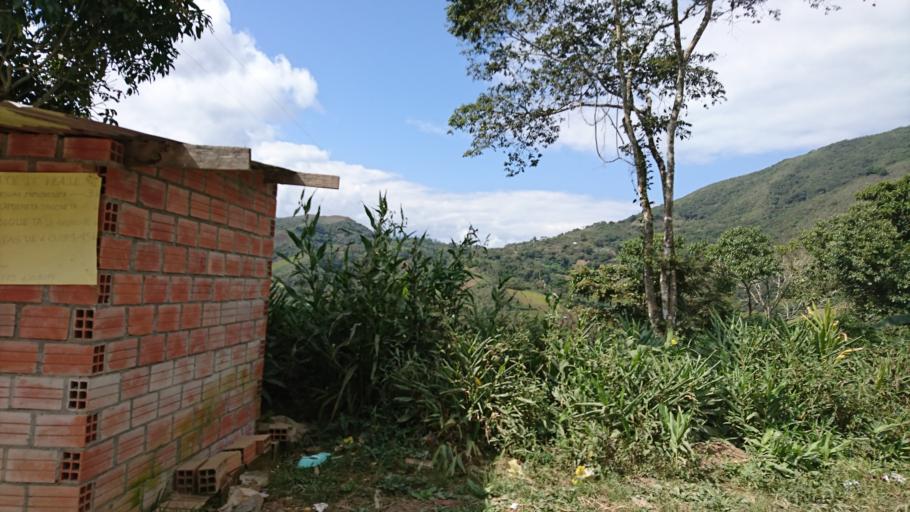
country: BO
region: La Paz
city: Coroico
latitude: -16.1229
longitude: -67.7626
